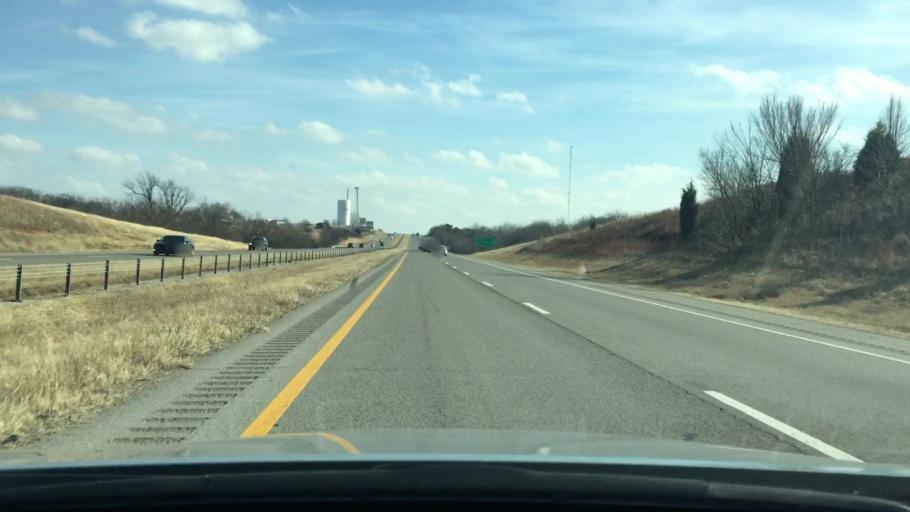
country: US
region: Oklahoma
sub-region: Cleveland County
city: Noble
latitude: 35.0720
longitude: -97.4011
